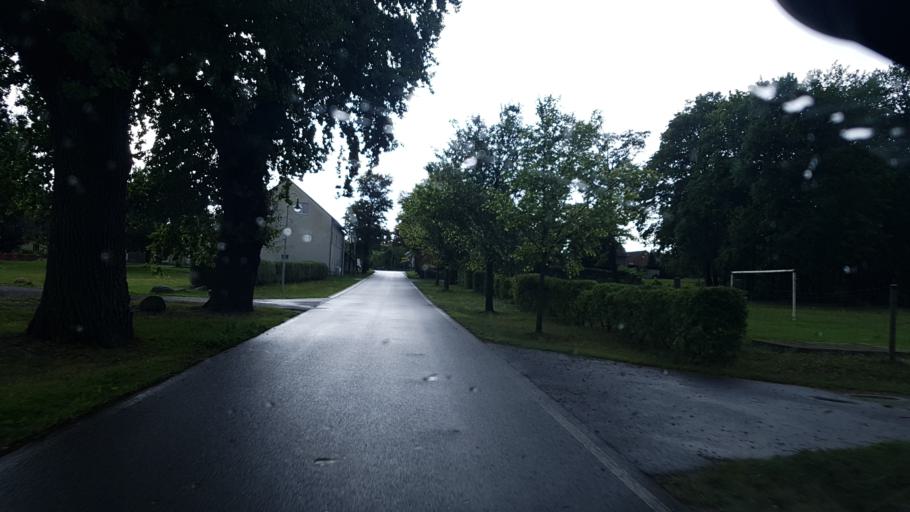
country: DE
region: Saxony
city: Gross Duben
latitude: 51.6237
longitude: 14.5350
